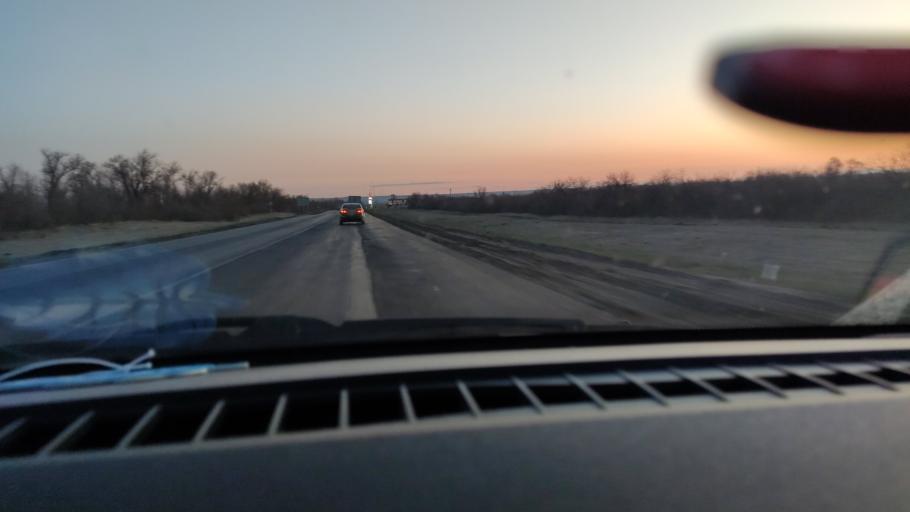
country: RU
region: Saratov
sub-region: Saratovskiy Rayon
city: Saratov
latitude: 51.6771
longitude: 46.0011
